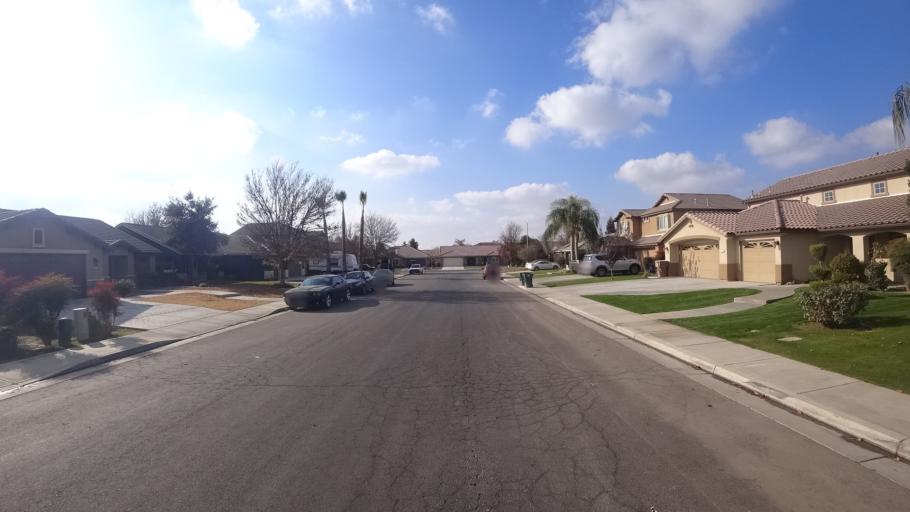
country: US
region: California
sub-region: Kern County
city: Greenacres
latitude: 35.3005
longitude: -119.1030
